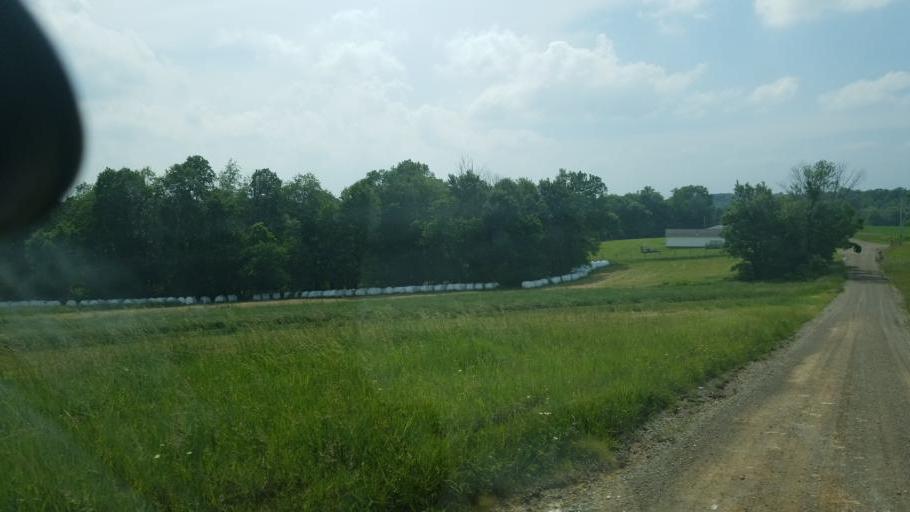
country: US
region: Ohio
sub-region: Muskingum County
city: Frazeysburg
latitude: 40.2492
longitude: -82.1850
